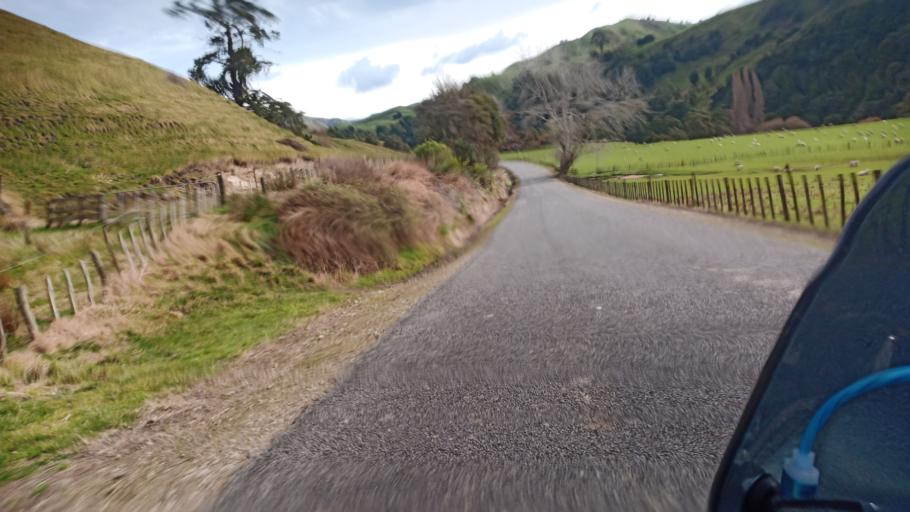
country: NZ
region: Hawke's Bay
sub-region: Wairoa District
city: Wairoa
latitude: -38.8001
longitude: 177.4680
